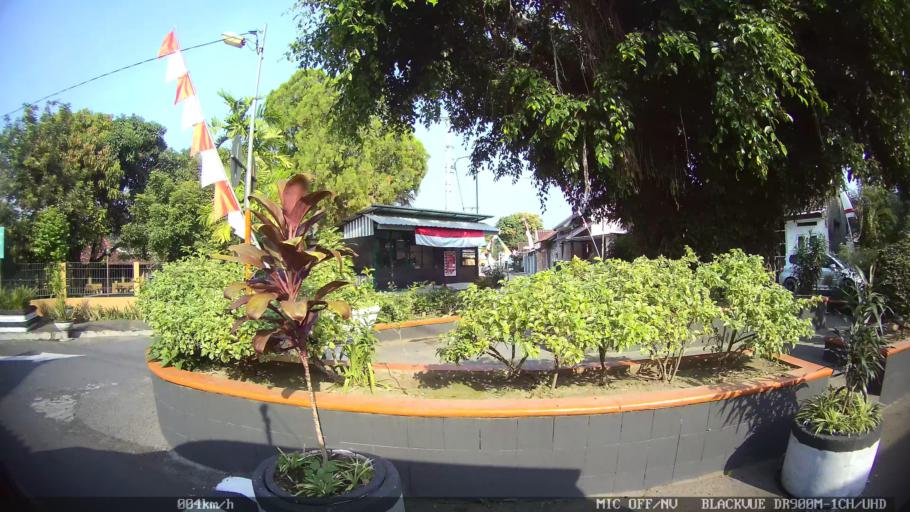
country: ID
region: Daerah Istimewa Yogyakarta
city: Yogyakarta
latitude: -7.8068
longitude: 110.3653
